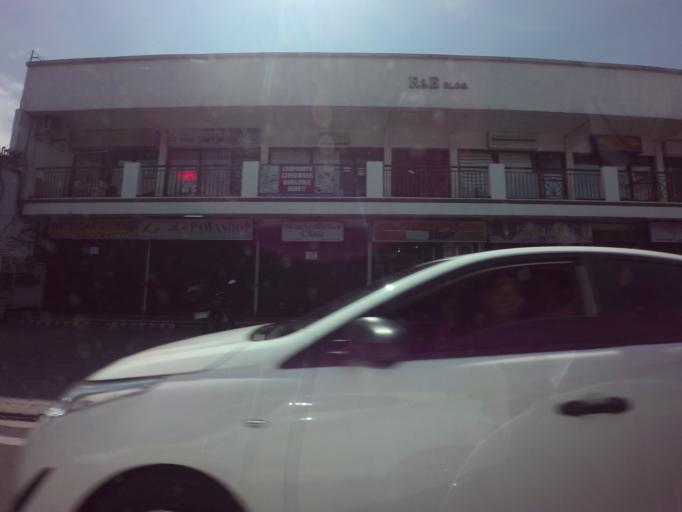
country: PH
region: Calabarzon
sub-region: Province of Rizal
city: Las Pinas
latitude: 14.4542
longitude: 120.9764
